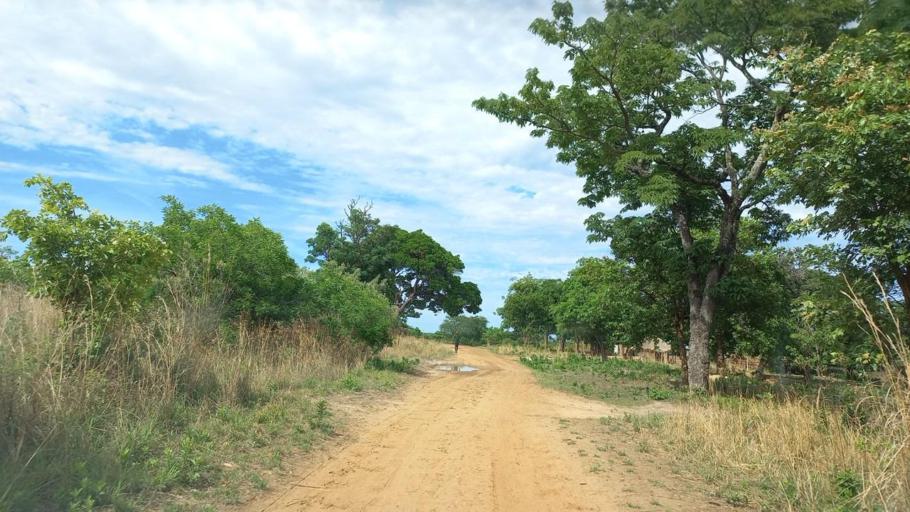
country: ZM
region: North-Western
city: Kabompo
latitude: -13.5089
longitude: 24.3956
